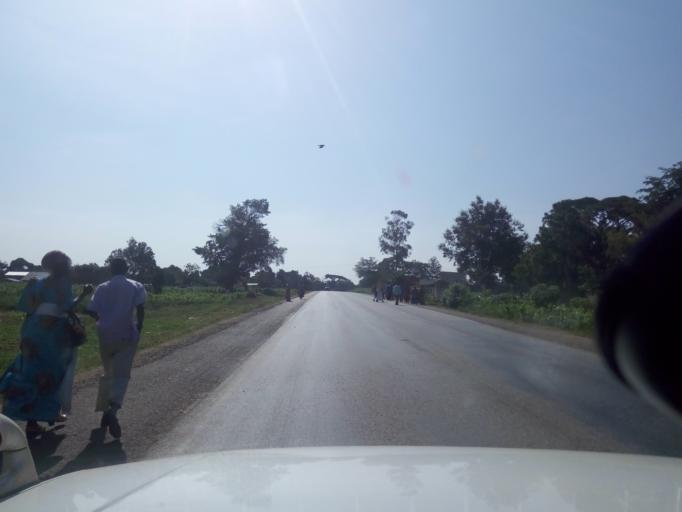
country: UG
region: Eastern Region
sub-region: Iganga District
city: Iganga
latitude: 0.6262
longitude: 33.6028
